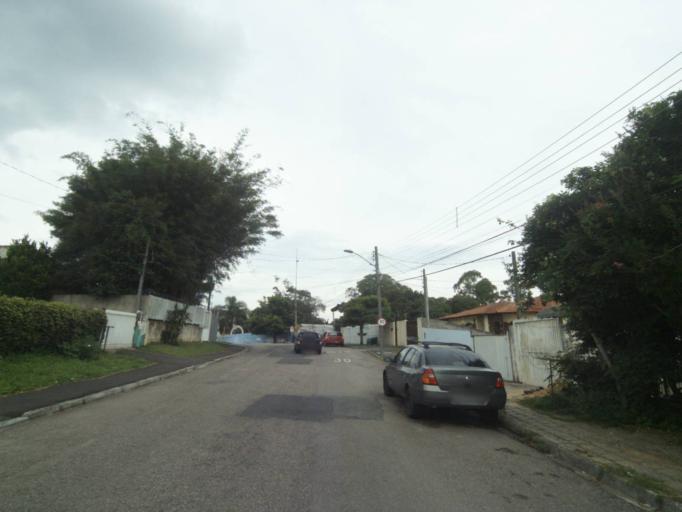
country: BR
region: Parana
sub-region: Curitiba
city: Curitiba
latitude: -25.3993
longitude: -49.2985
